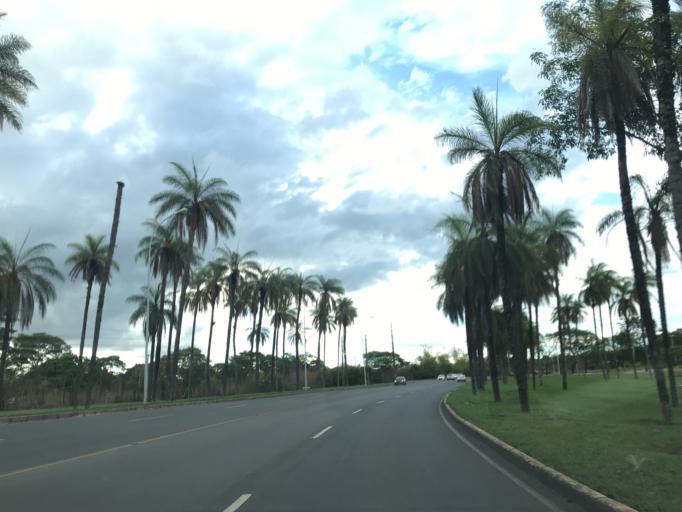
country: BR
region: Federal District
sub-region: Brasilia
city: Brasilia
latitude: -15.8141
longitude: -47.9248
